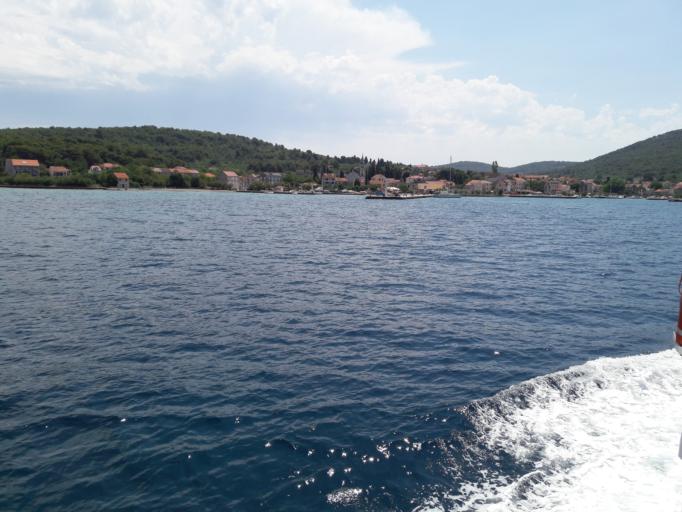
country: HR
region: Sibensko-Kniniska
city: Vodice
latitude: 43.7008
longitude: 15.8311
